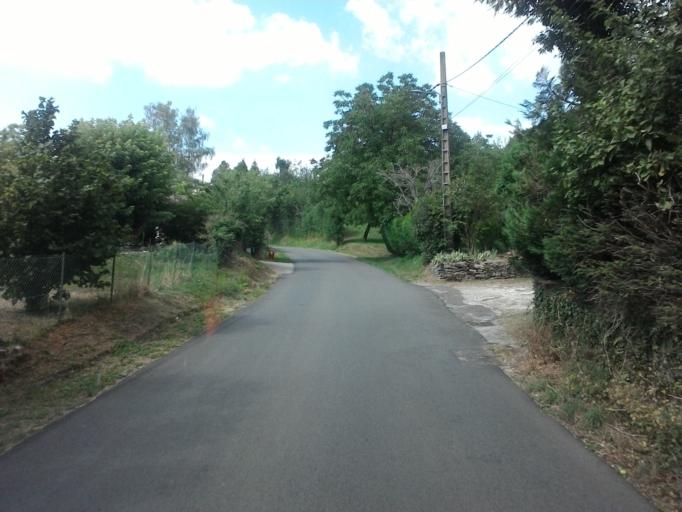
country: FR
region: Franche-Comte
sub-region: Departement du Doubs
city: Quingey
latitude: 47.1100
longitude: 5.9155
